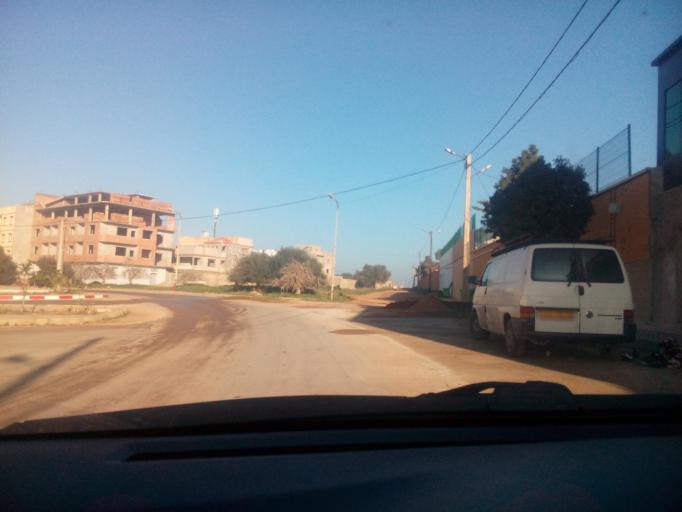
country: DZ
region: Oran
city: Bir el Djir
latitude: 35.7550
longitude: -0.5302
